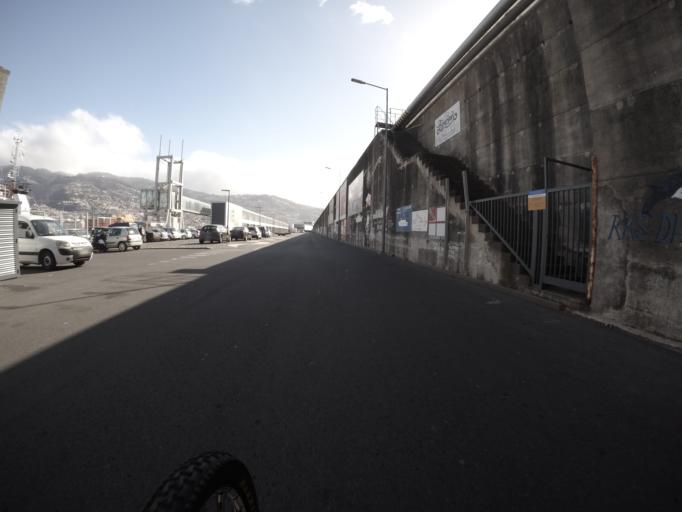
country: PT
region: Madeira
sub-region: Funchal
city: Funchal
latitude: 32.6412
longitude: -16.9144
